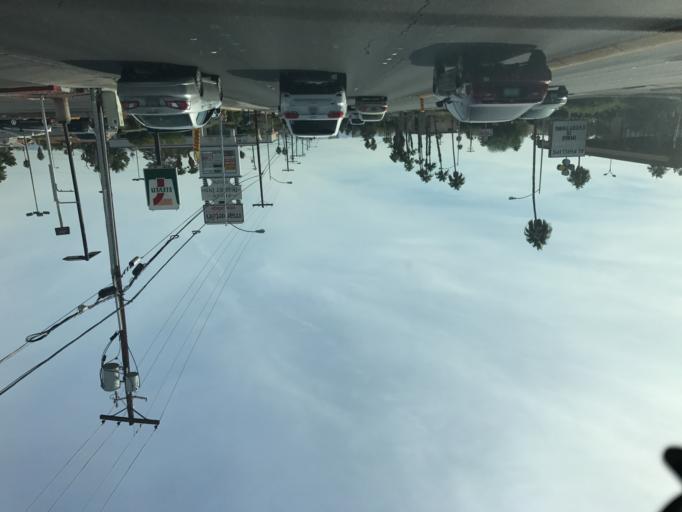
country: US
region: Nevada
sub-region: Clark County
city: Winchester
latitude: 36.1297
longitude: -115.0921
